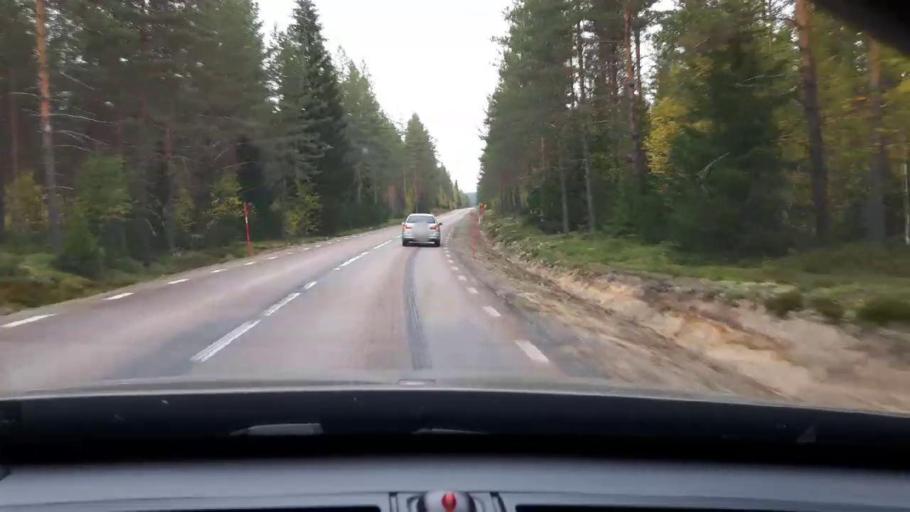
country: SE
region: Dalarna
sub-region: Gagnefs Kommun
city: Mockfjard
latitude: 60.3742
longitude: 14.8077
